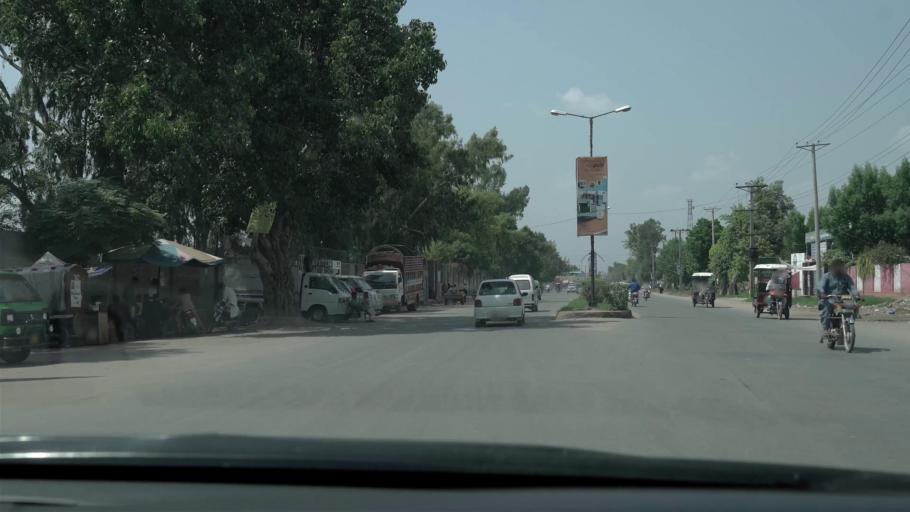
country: PK
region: Punjab
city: Gojra
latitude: 31.1531
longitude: 72.6731
